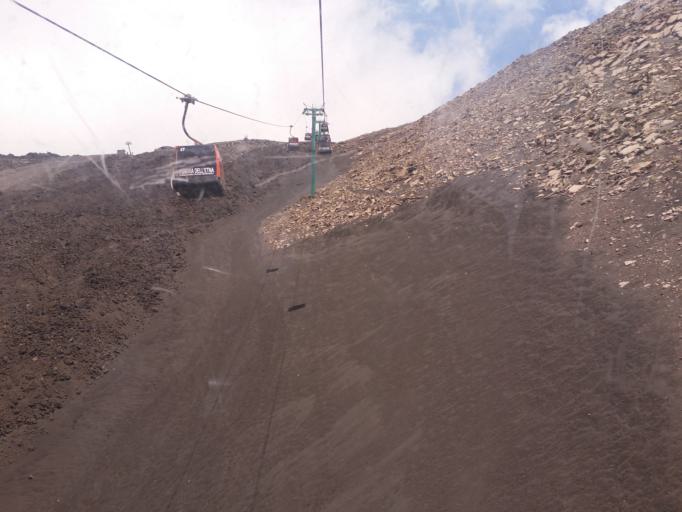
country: IT
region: Sicily
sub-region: Catania
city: Ragalna
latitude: 37.7146
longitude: 14.9998
